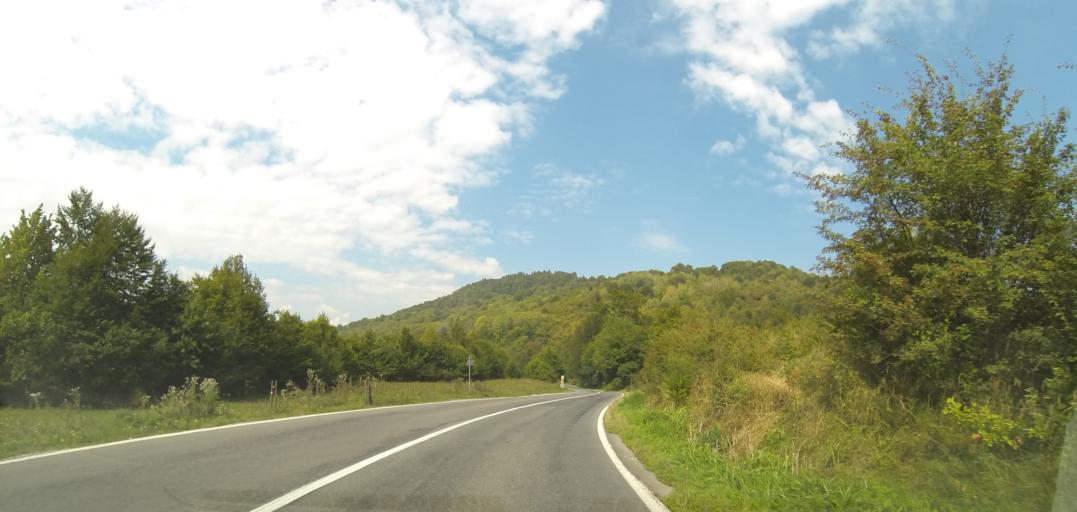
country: RO
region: Brasov
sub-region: Comuna Tarlungeni
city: Zizin
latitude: 45.5548
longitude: 25.8038
